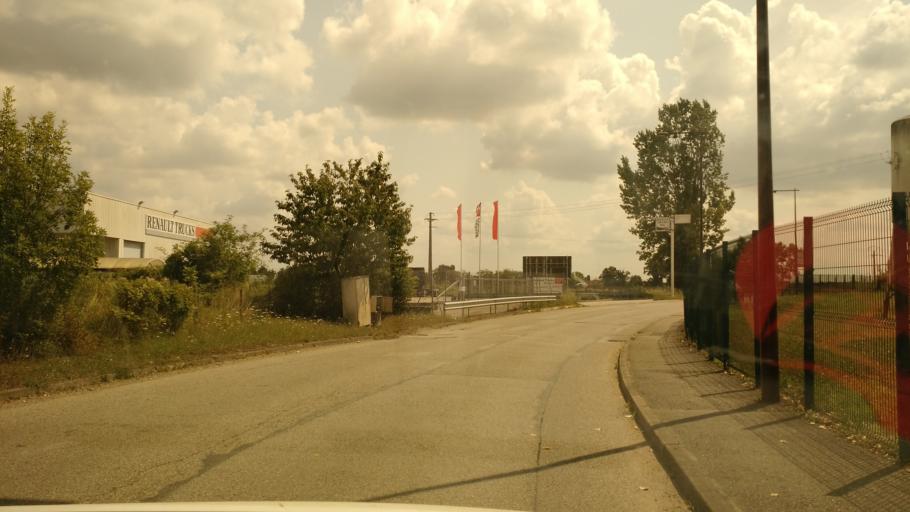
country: FR
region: Rhone-Alpes
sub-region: Departement de l'Ain
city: Montluel
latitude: 45.8432
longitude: 5.0585
